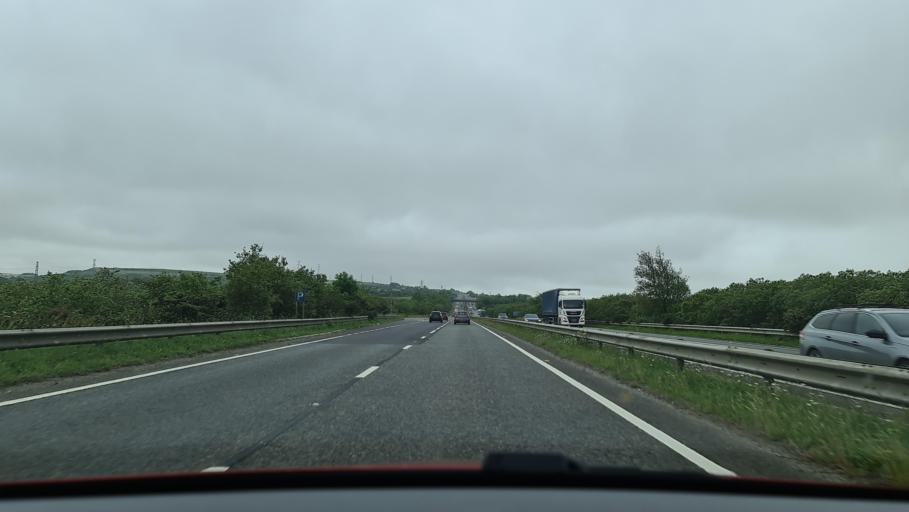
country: GB
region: England
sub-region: Cornwall
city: Saint Dennis
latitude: 50.4028
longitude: -4.9086
